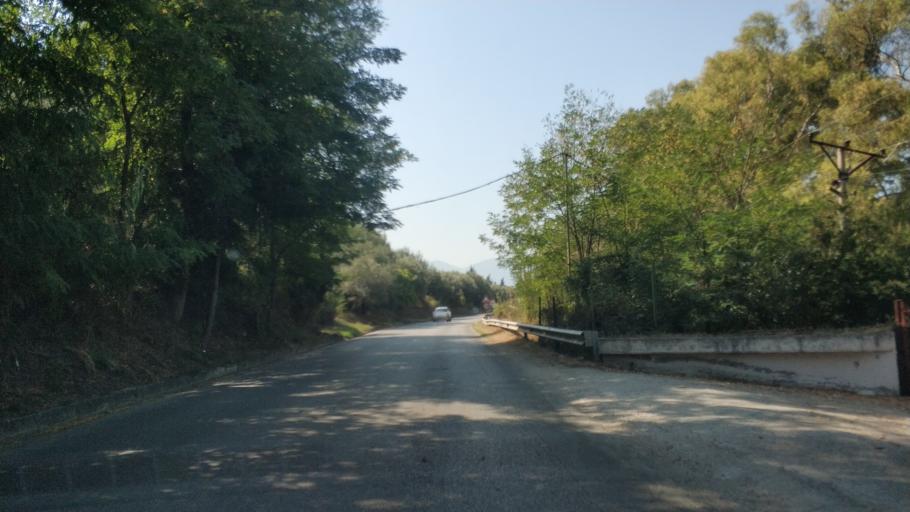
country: AL
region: Vlore
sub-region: Rrethi i Vlores
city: Orikum
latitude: 40.3823
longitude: 19.4843
